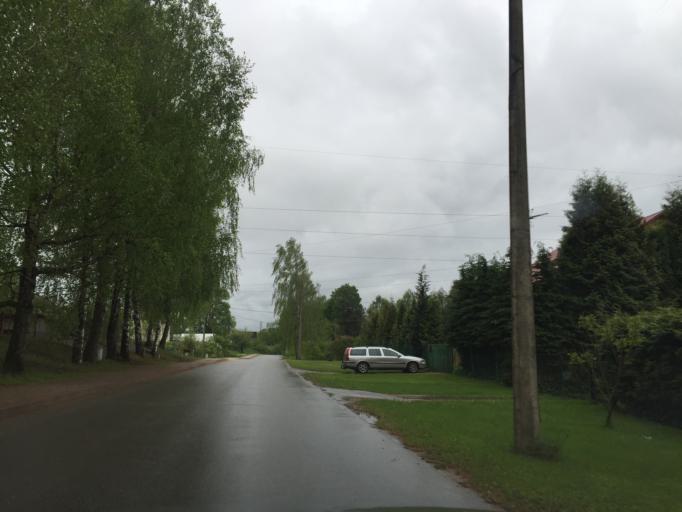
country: LV
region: Kegums
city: Kegums
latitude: 56.7470
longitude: 24.7209
